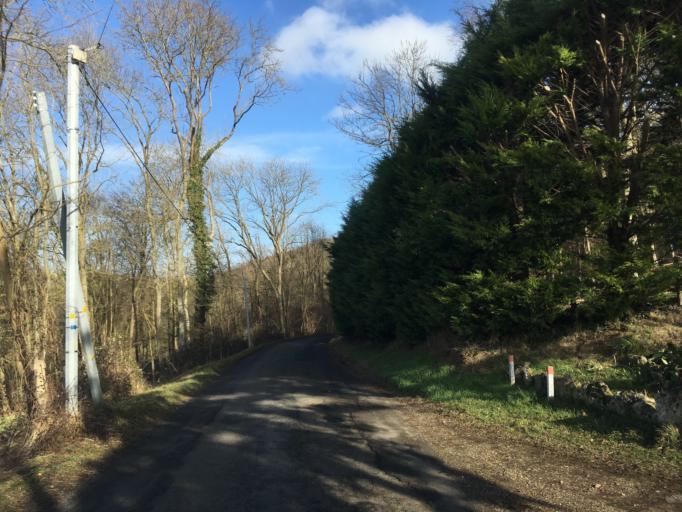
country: FR
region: Haute-Normandie
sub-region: Departement de l'Eure
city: La Chapelle-Reanville
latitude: 49.1282
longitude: 1.4063
